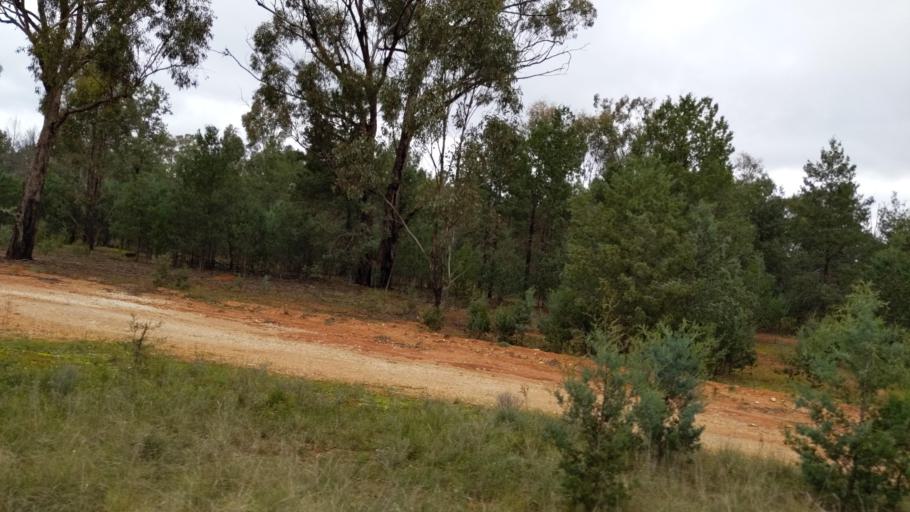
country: AU
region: New South Wales
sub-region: Coolamon
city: Coolamon
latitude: -34.8236
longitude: 146.9119
